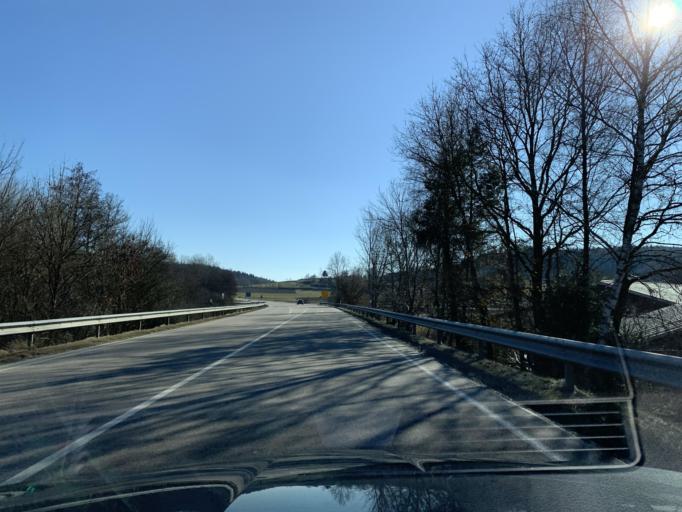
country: DE
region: Bavaria
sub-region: Upper Palatinate
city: Pemfling
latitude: 49.3022
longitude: 12.6292
